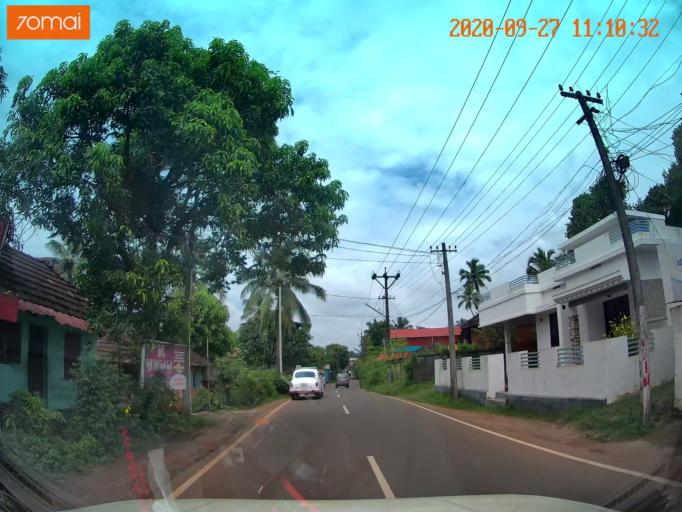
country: IN
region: Kerala
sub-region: Thrissur District
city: Trichur
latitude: 10.4305
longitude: 76.2194
